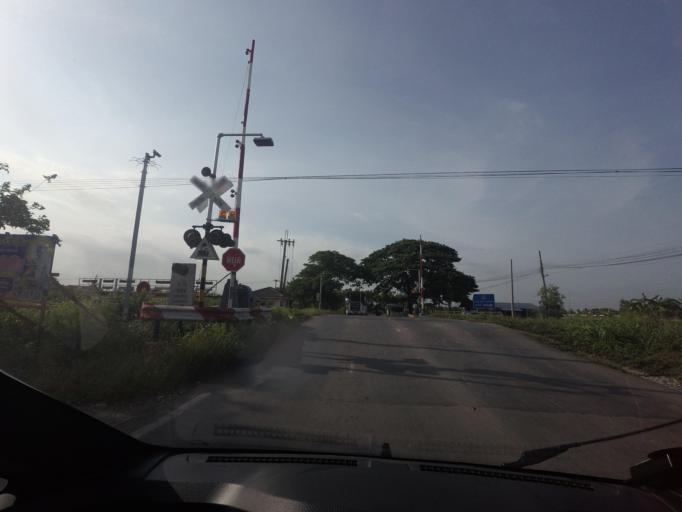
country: TH
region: Bangkok
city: Lat Krabang
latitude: 13.7208
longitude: 100.8556
